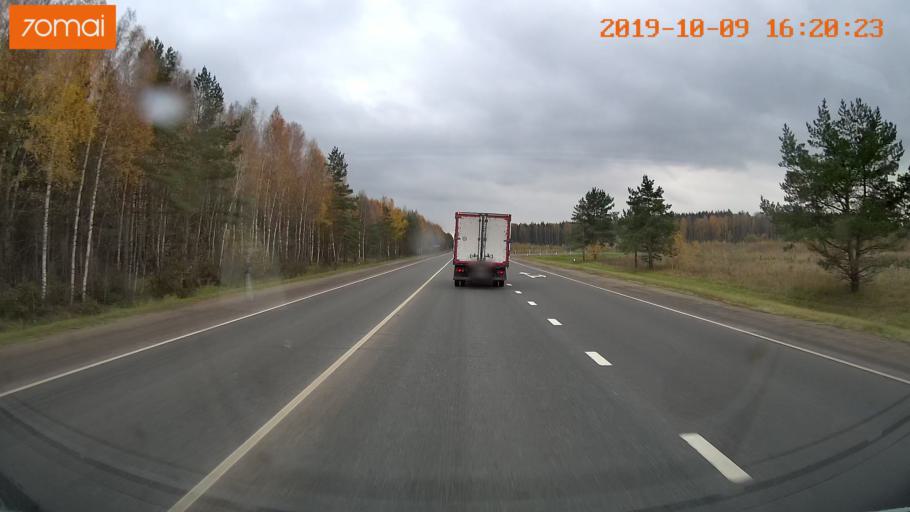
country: RU
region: Kostroma
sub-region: Kostromskoy Rayon
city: Kostroma
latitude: 57.7071
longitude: 40.8923
